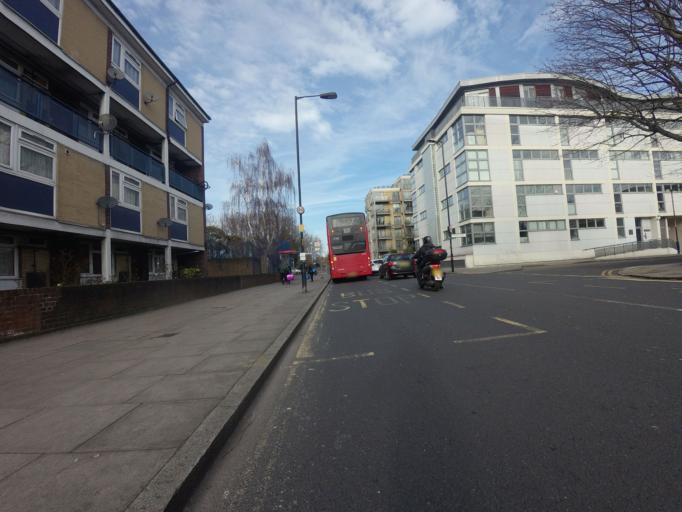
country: GB
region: England
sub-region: Greater London
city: Camberwell
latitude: 51.4817
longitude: -0.0741
